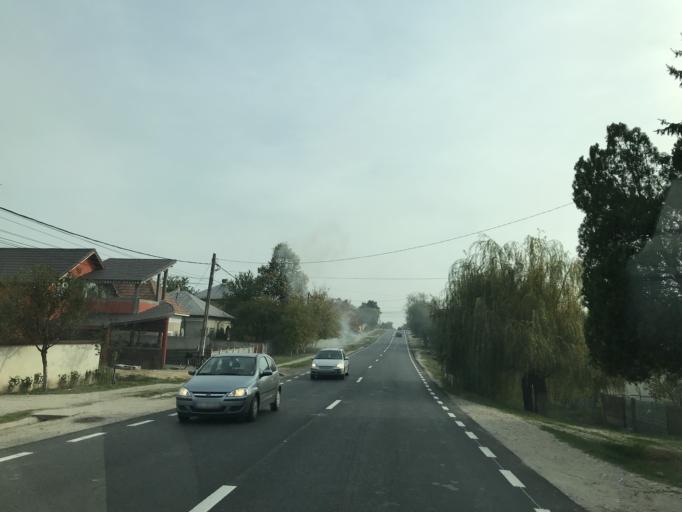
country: RO
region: Olt
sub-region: Comuna Piatra Olt
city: Piatra
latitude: 44.3637
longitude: 24.2930
